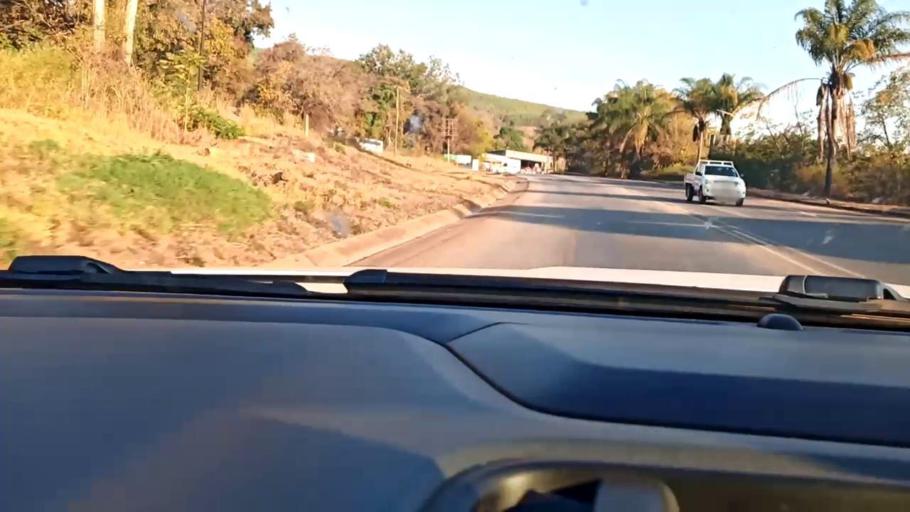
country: ZA
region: Limpopo
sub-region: Mopani District Municipality
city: Duiwelskloof
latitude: -23.6907
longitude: 30.1464
